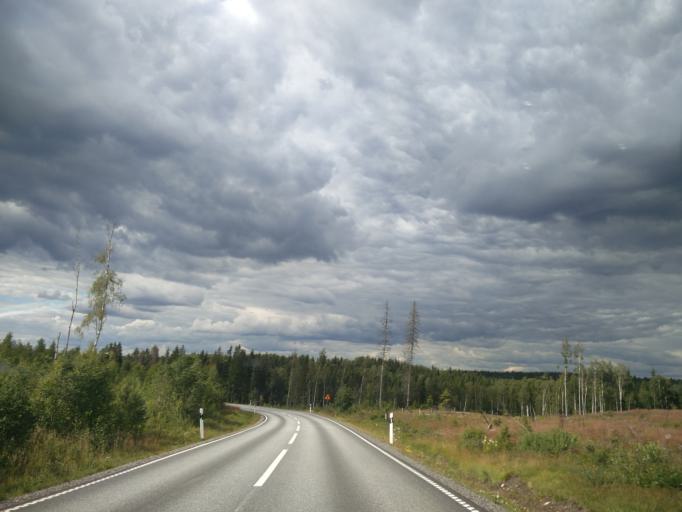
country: SE
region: OErebro
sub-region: Hallefors Kommun
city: Haellefors
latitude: 59.8148
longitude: 14.6614
